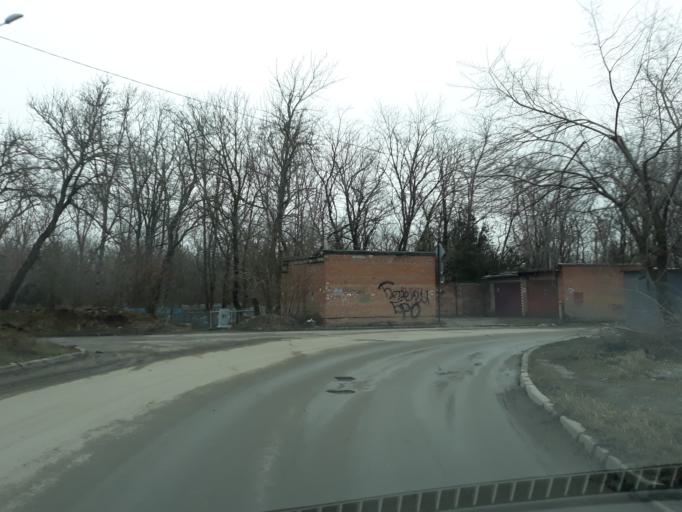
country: RU
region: Rostov
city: Taganrog
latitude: 47.2081
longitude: 38.8988
